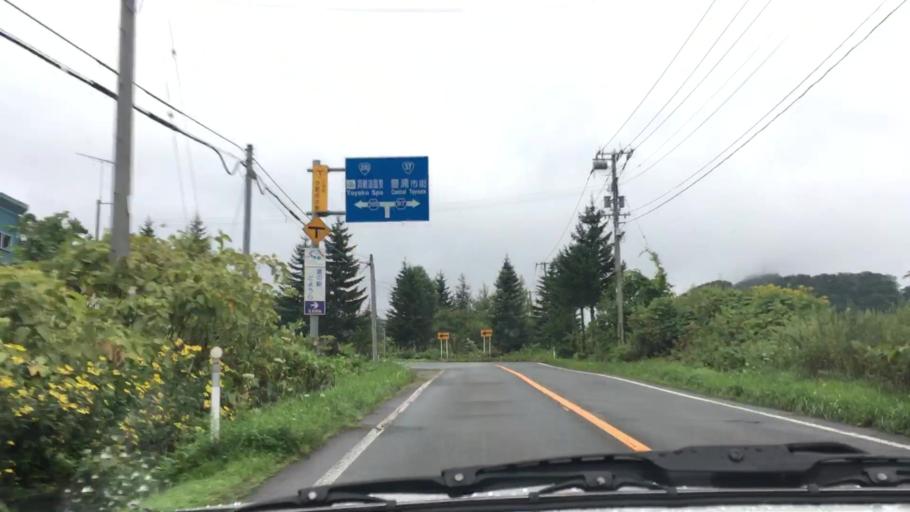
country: JP
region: Hokkaido
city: Niseko Town
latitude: 42.6098
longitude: 140.7273
